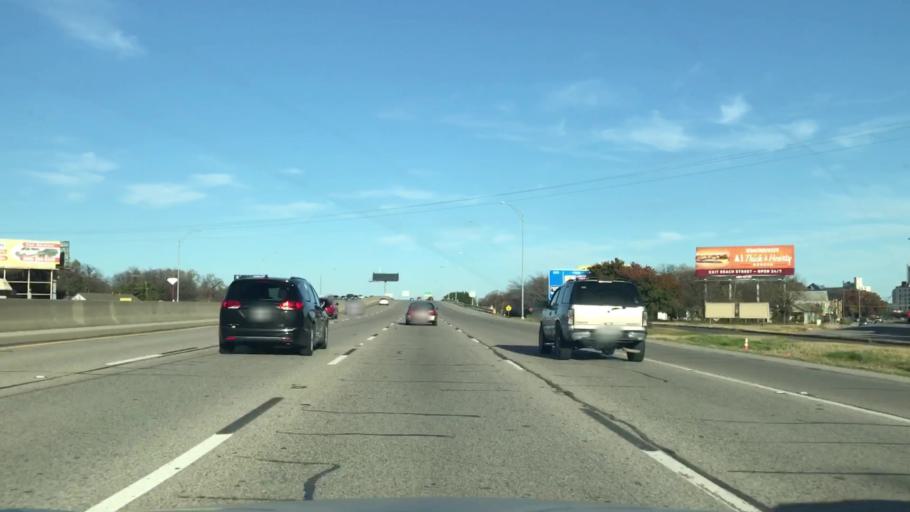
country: US
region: Texas
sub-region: Tarrant County
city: Haltom City
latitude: 32.7699
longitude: -97.2984
